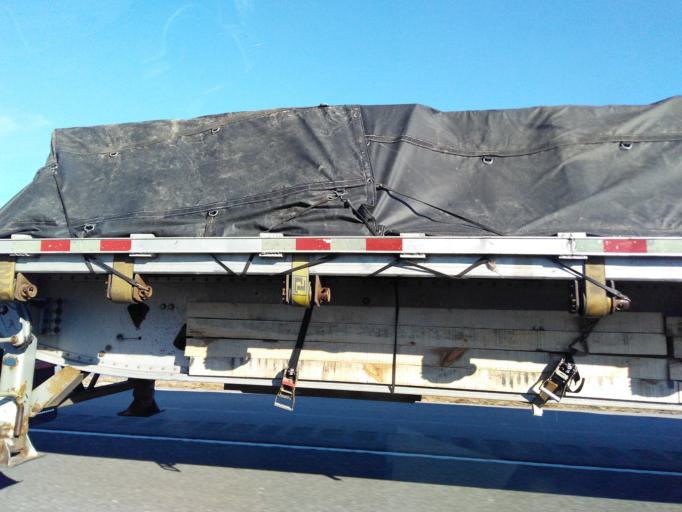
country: US
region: Illinois
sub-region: Williamson County
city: Johnston City
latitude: 37.8055
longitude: -88.9457
